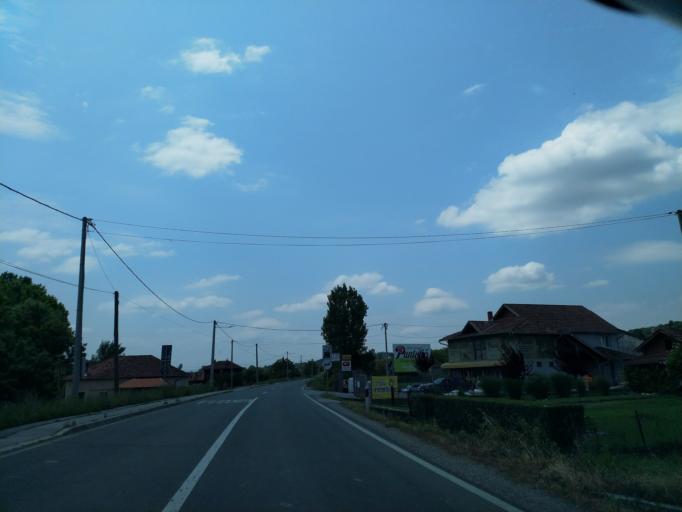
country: RS
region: Central Serbia
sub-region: Rasinski Okrug
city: Krusevac
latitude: 43.4997
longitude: 21.2932
